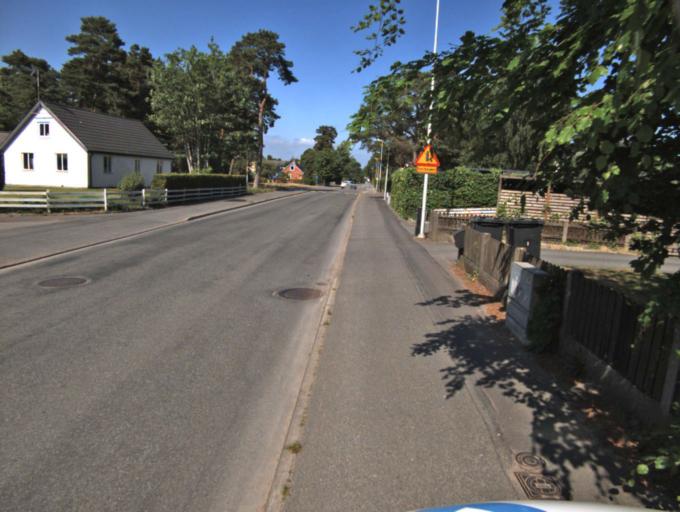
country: SE
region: Skane
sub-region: Kristianstads Kommun
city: Ahus
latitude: 55.9161
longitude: 14.2881
